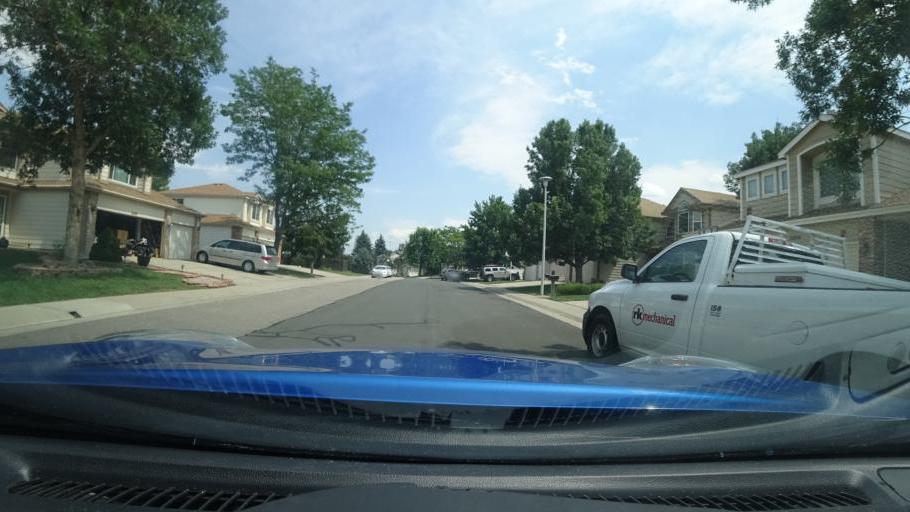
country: US
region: Colorado
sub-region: Adams County
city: Aurora
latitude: 39.6725
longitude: -104.7742
